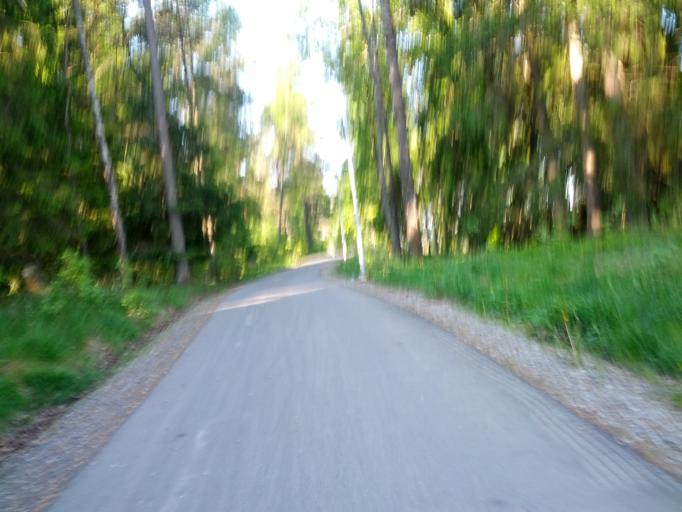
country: SE
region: Stockholm
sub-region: Taby Kommun
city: Taby
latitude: 59.4810
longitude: 18.0611
